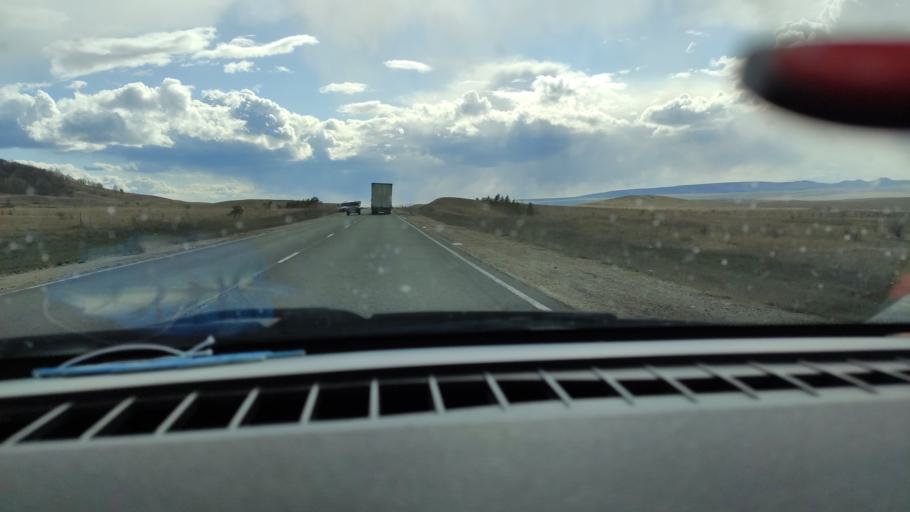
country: RU
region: Saratov
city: Alekseyevka
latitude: 52.3601
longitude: 47.9525
